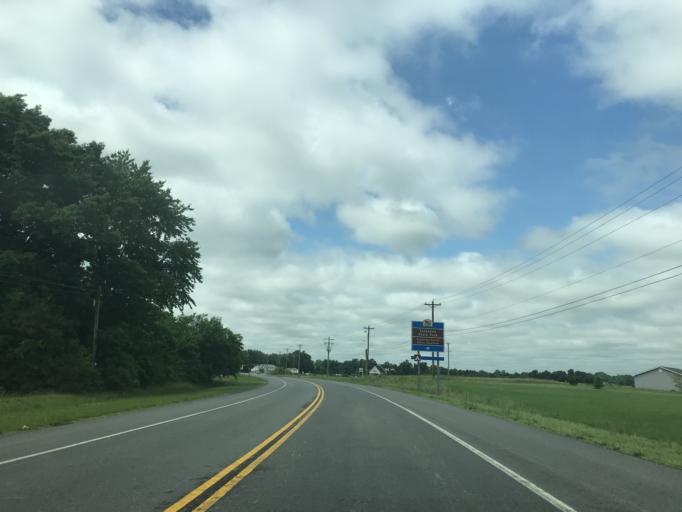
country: US
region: Maryland
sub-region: Caroline County
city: Ridgely
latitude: 38.9240
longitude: -75.9328
